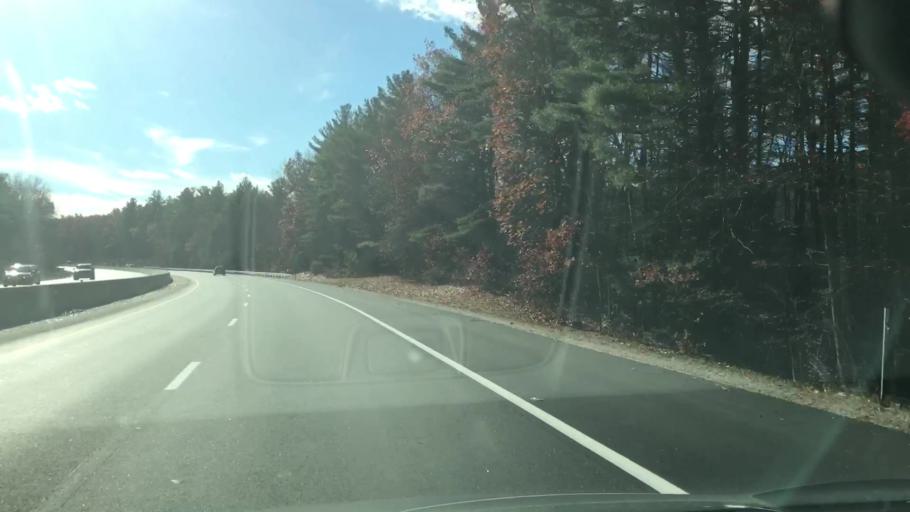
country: US
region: New Hampshire
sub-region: Hillsborough County
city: Pinardville
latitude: 43.0363
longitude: -71.4841
